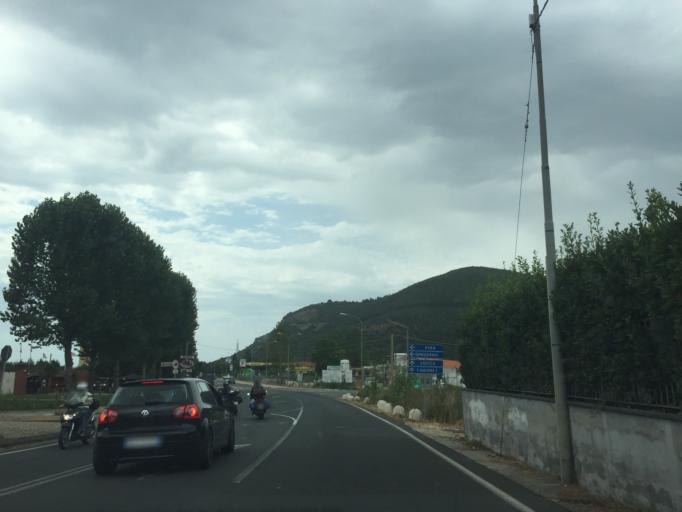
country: IT
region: Tuscany
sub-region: Province of Pisa
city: Asciano
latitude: 43.7477
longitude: 10.4636
